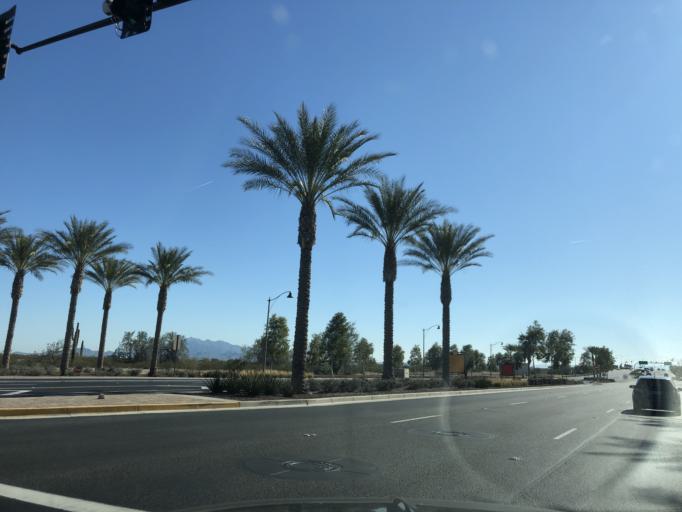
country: US
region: Arizona
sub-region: Maricopa County
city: Citrus Park
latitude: 33.4667
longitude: -112.5045
